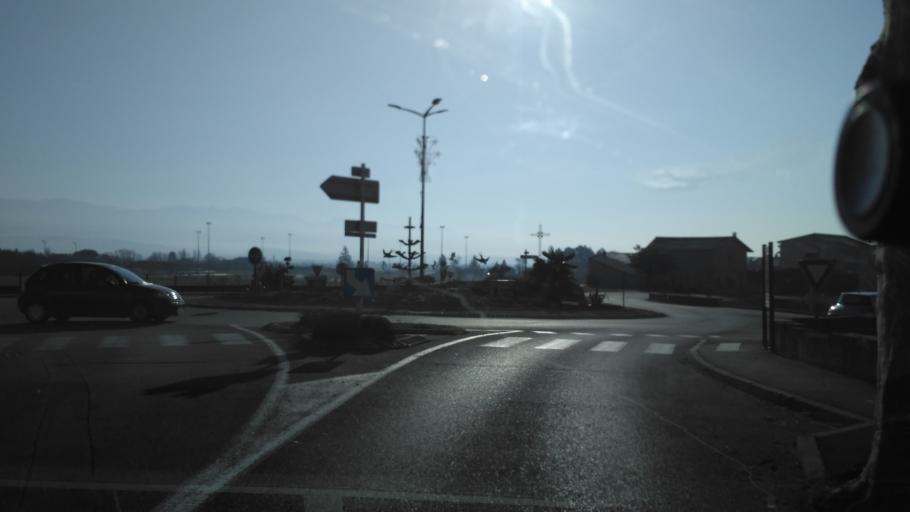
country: FR
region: Rhone-Alpes
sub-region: Departement de la Drome
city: Genissieux
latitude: 45.0823
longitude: 5.0871
